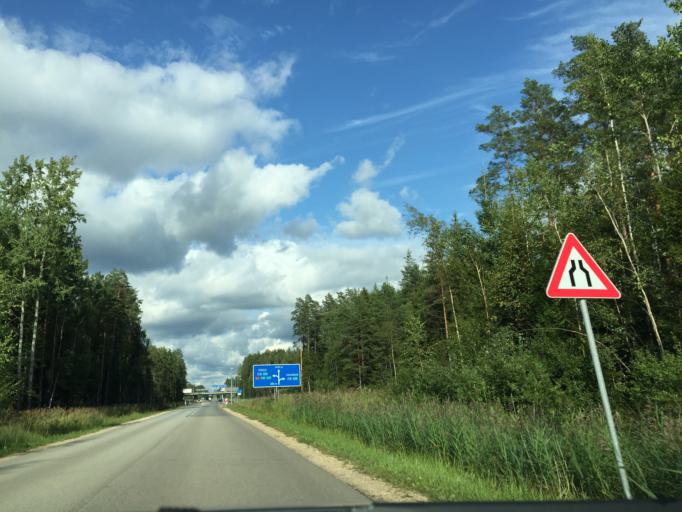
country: LV
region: Ogre
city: Ogre
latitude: 56.8410
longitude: 24.6679
